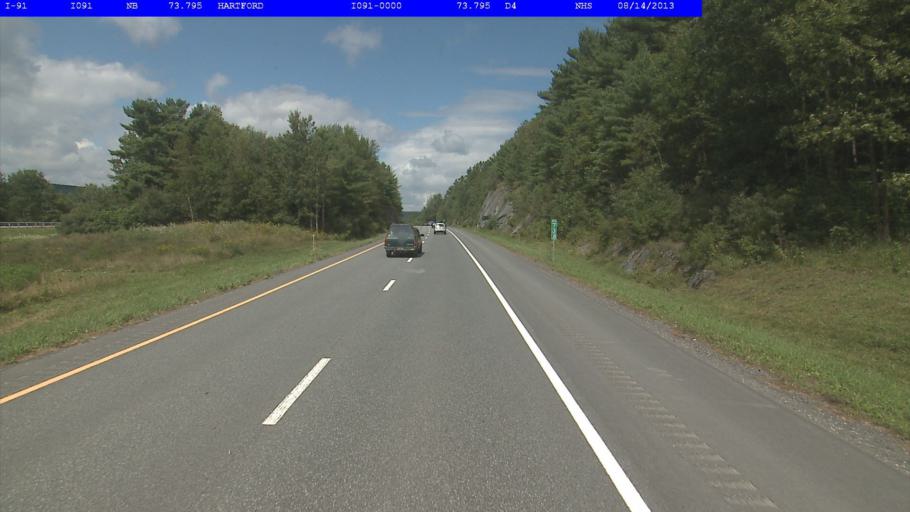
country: US
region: Vermont
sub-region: Windsor County
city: Wilder
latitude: 43.6914
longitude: -72.3112
